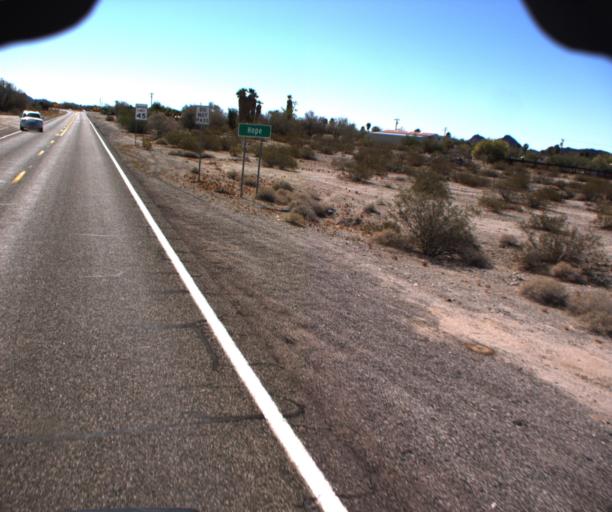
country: US
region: Arizona
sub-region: La Paz County
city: Salome
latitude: 33.7253
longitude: -113.7067
